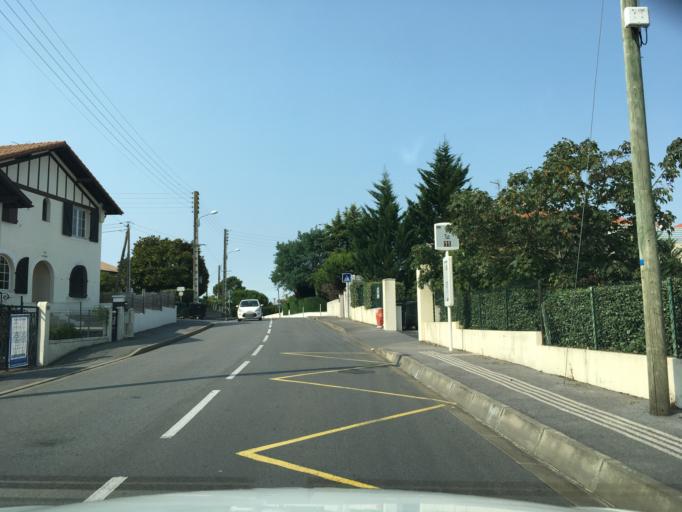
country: FR
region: Aquitaine
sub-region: Departement des Pyrenees-Atlantiques
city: Bayonne
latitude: 43.5090
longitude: -1.5025
